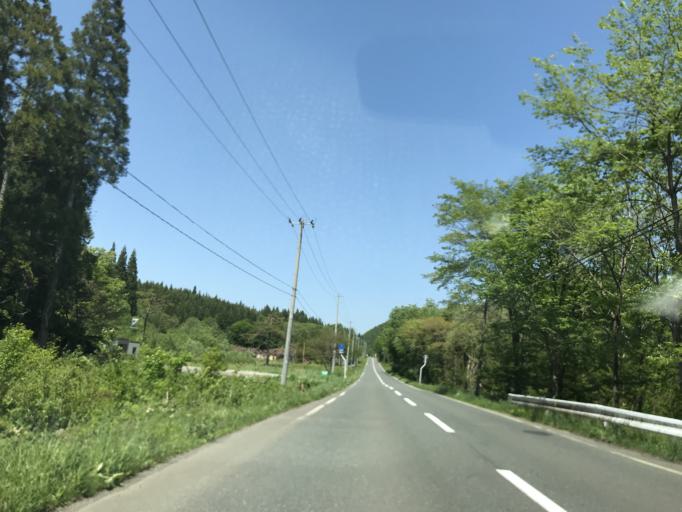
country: JP
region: Iwate
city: Shizukuishi
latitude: 39.5253
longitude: 140.8287
